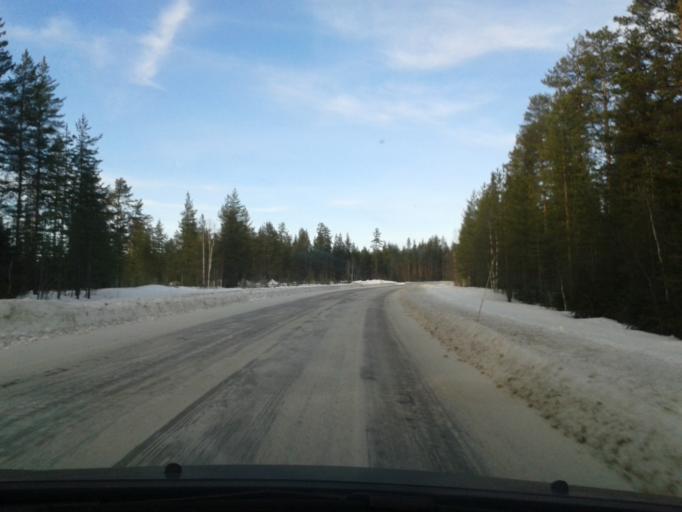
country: SE
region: Vaesternorrland
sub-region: OErnskoeldsviks Kommun
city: Bredbyn
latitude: 63.6075
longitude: 17.8998
